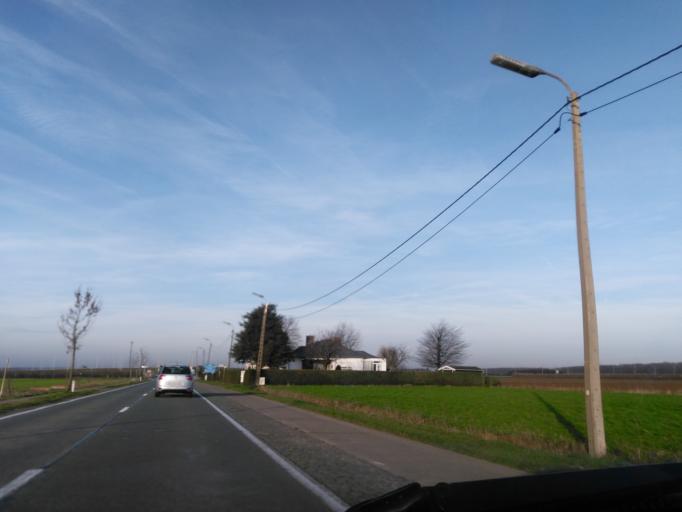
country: BE
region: Flanders
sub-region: Provincie Oost-Vlaanderen
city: Sint-Gillis-Waas
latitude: 51.2333
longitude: 4.1904
